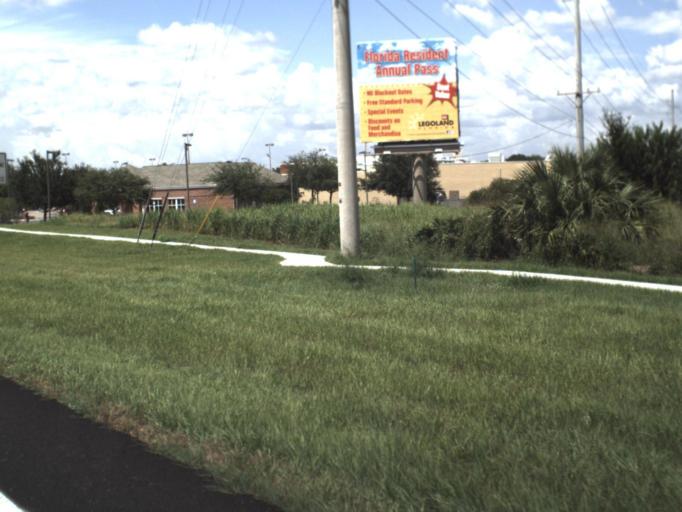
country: US
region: Florida
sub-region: Polk County
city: Cypress Gardens
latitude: 27.9852
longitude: -81.6853
